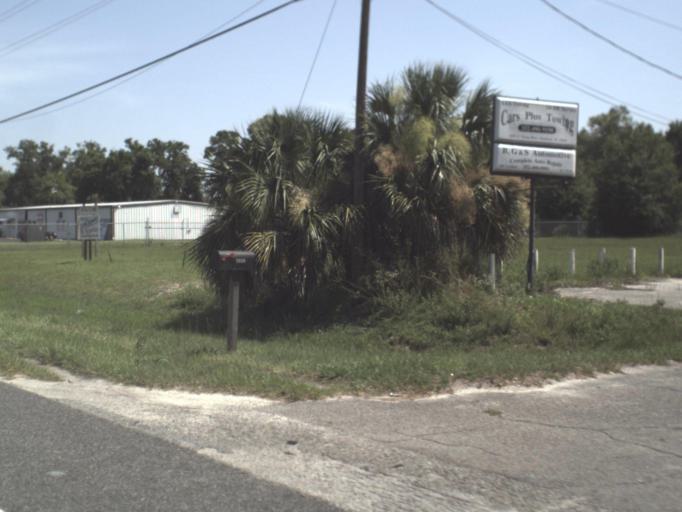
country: US
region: Florida
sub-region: Levy County
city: Manatee Road
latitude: 29.5117
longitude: -82.8761
